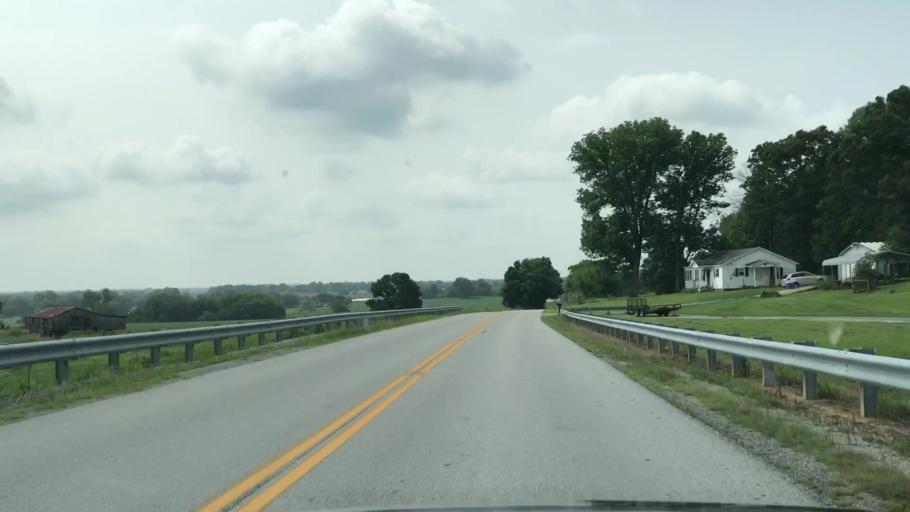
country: US
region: Kentucky
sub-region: Edmonson County
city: Brownsville
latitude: 37.1011
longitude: -86.1469
